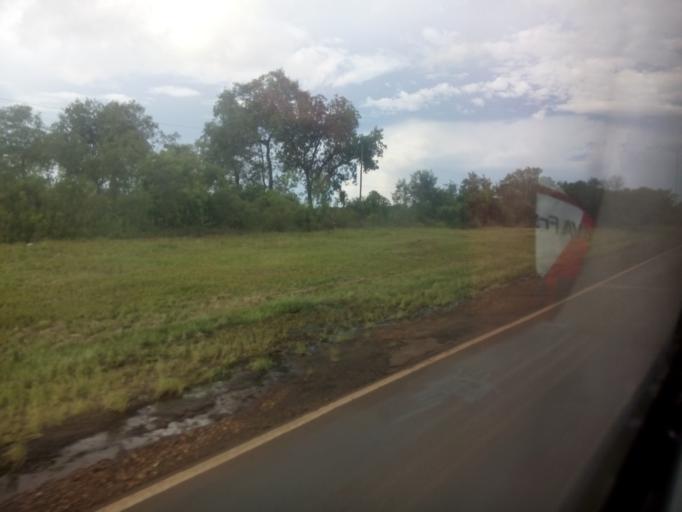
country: AR
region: Misiones
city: Santa Ana
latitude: -27.4299
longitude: -55.6324
